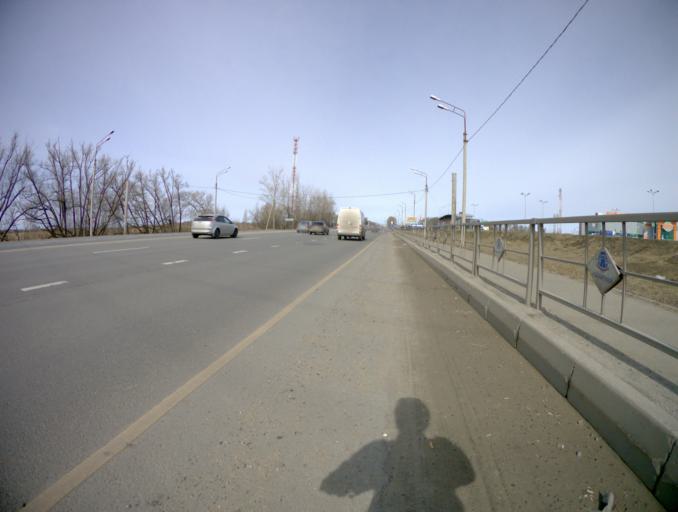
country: RU
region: Vladimir
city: Kommunar
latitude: 56.1752
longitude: 40.4570
